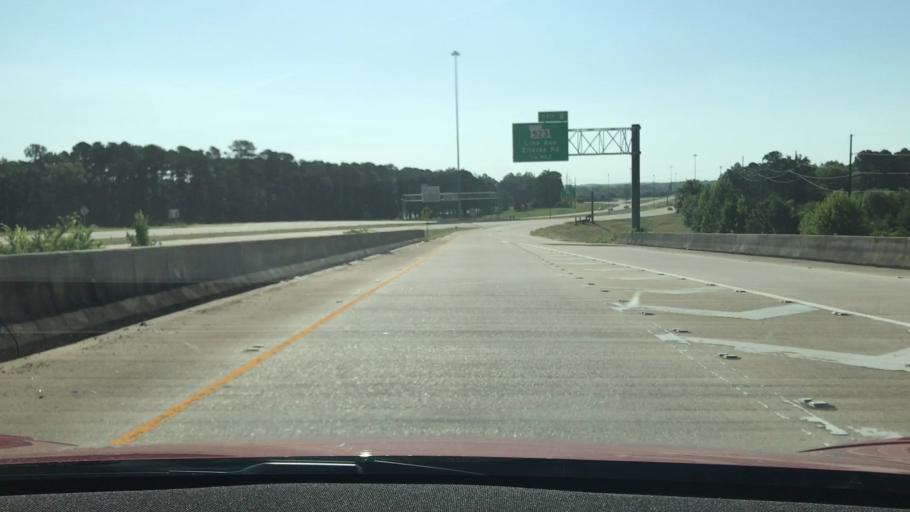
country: US
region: Louisiana
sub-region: Bossier Parish
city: Bossier City
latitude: 32.4180
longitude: -93.7459
